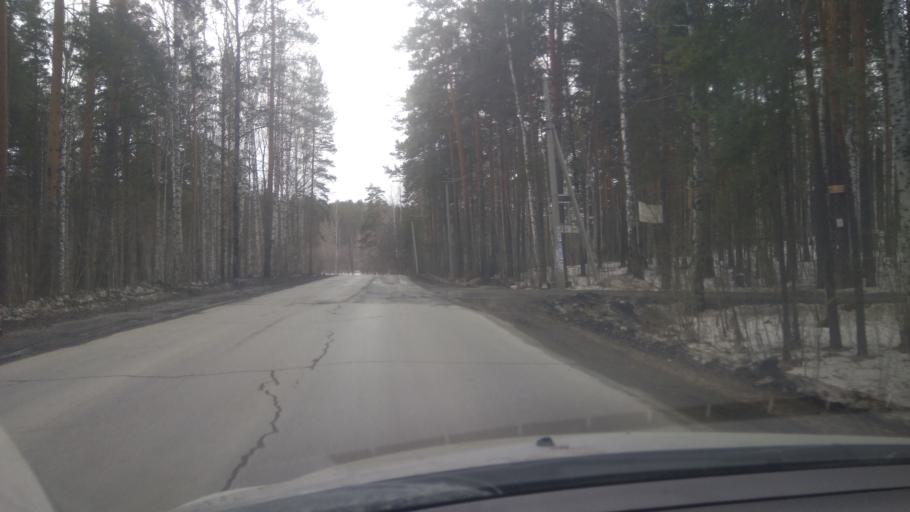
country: RU
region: Sverdlovsk
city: Severka
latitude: 56.8375
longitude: 60.3831
